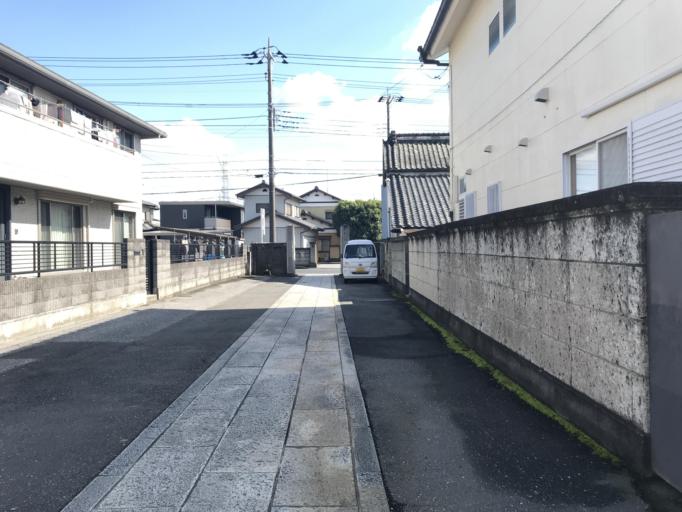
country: JP
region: Tochigi
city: Oyama
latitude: 36.2642
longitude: 139.7633
